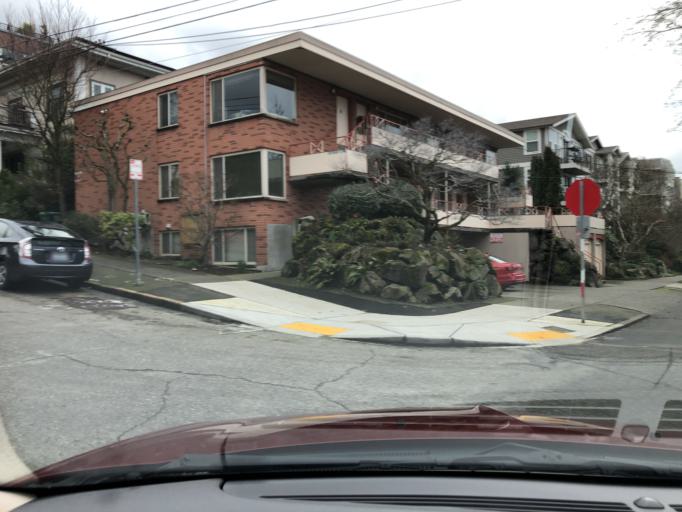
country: US
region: Washington
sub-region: King County
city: Seattle
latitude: 47.6399
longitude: -122.3271
